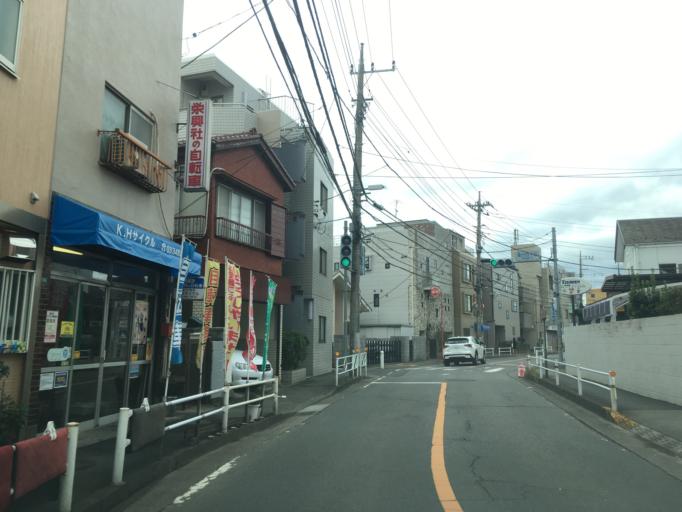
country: JP
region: Tokyo
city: Chofugaoka
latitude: 35.6240
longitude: 139.5784
